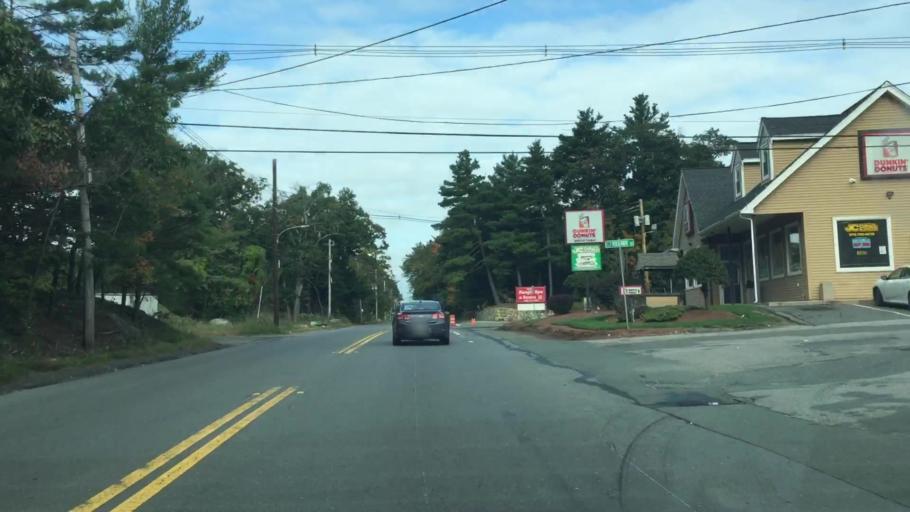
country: US
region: Massachusetts
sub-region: Essex County
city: Middleton
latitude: 42.6208
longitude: -71.0527
